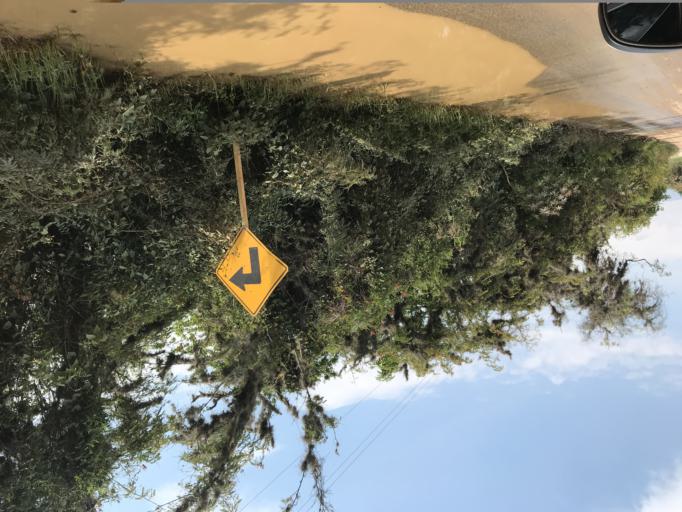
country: CO
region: Boyaca
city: Villa de Leiva
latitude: 5.6596
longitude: -73.5817
